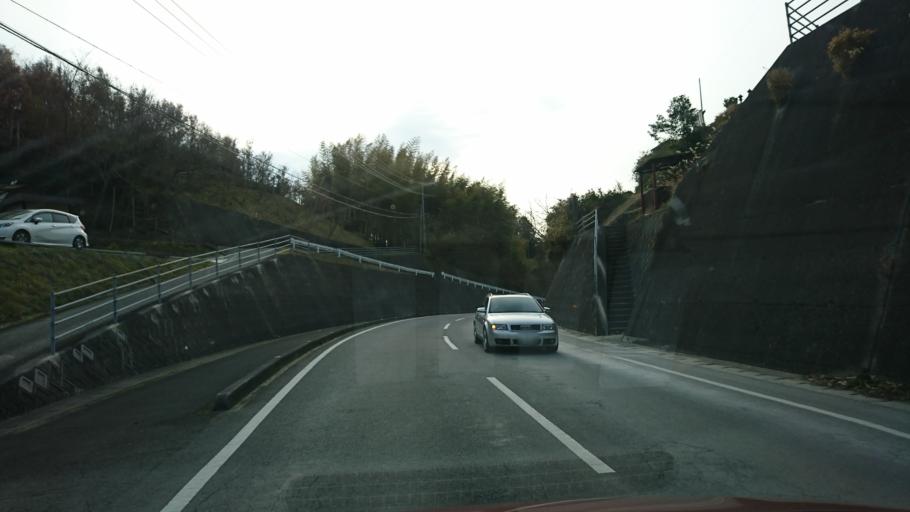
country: JP
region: Ehime
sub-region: Shikoku-chuo Shi
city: Matsuyama
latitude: 33.9022
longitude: 132.8103
